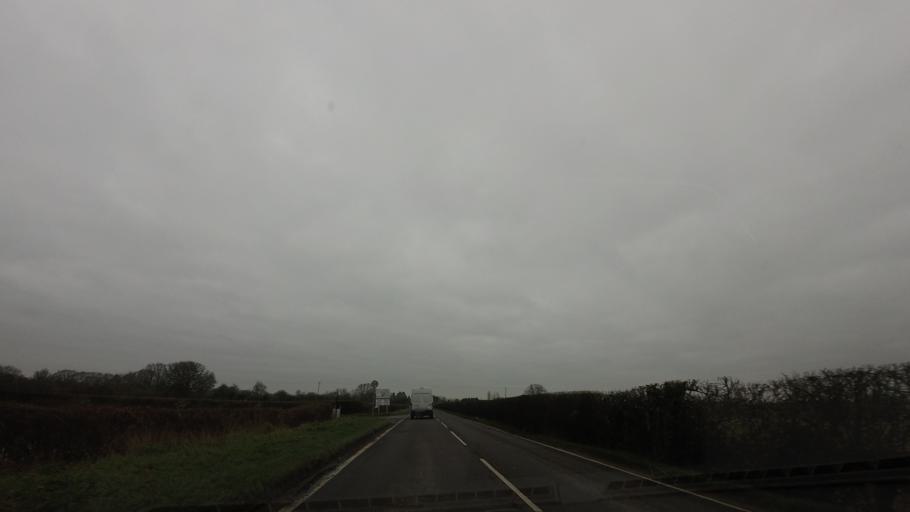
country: GB
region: England
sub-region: Kent
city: Staplehurst
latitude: 51.1347
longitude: 0.5577
